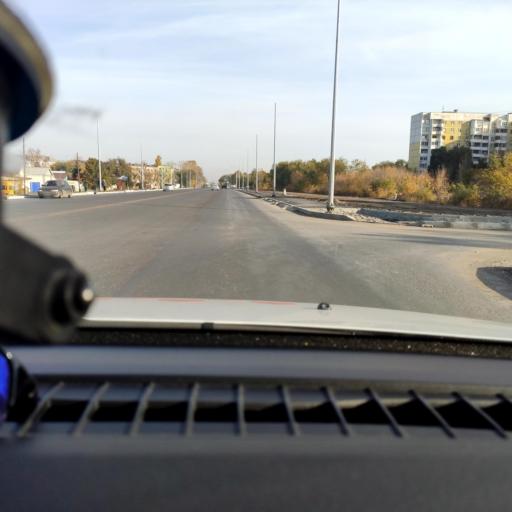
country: RU
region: Samara
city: Samara
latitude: 53.1119
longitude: 50.0828
